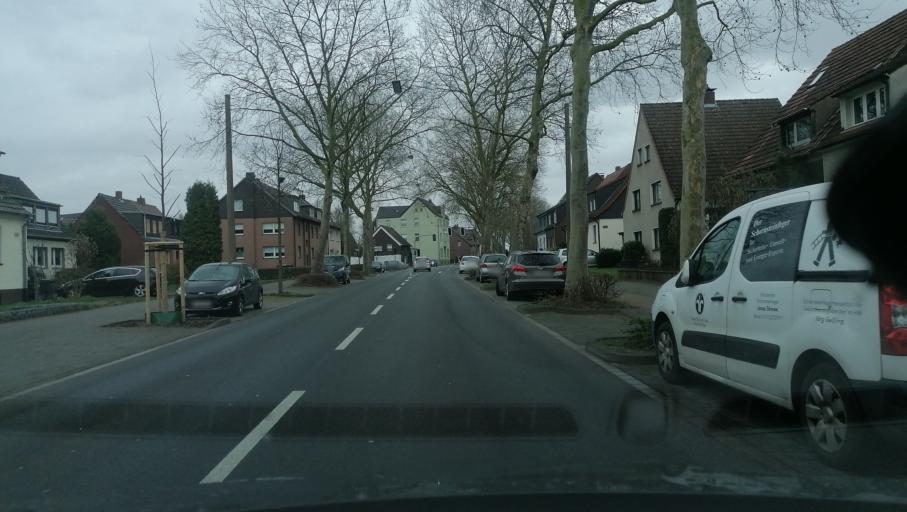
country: DE
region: North Rhine-Westphalia
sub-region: Regierungsbezirk Munster
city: Recklinghausen
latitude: 51.6024
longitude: 7.2207
